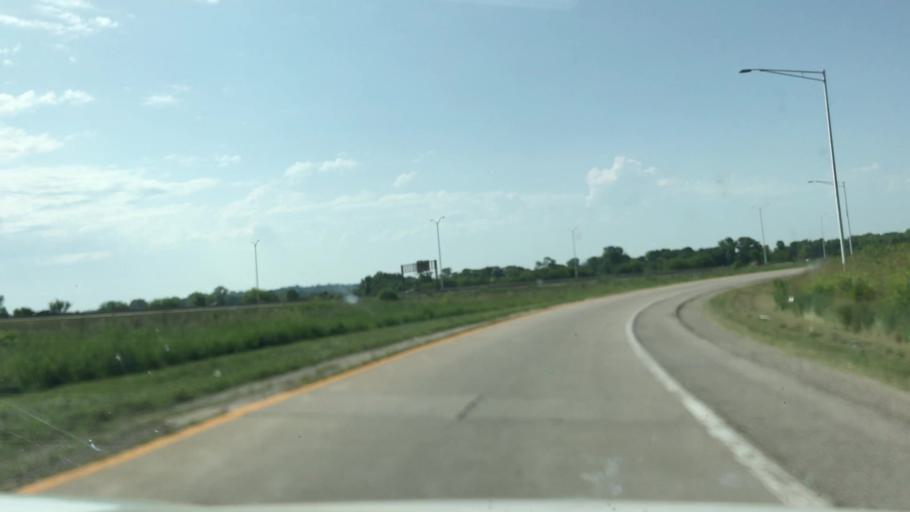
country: US
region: Illinois
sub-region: Saint Clair County
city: Washington Park
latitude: 38.6172
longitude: -90.0721
